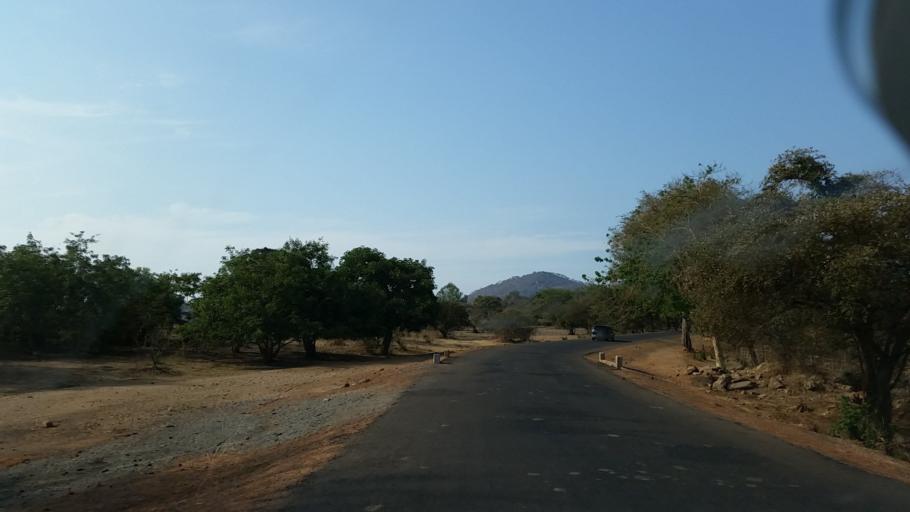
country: MW
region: Central Region
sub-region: Salima District
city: Salima
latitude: -13.7044
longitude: 34.5896
